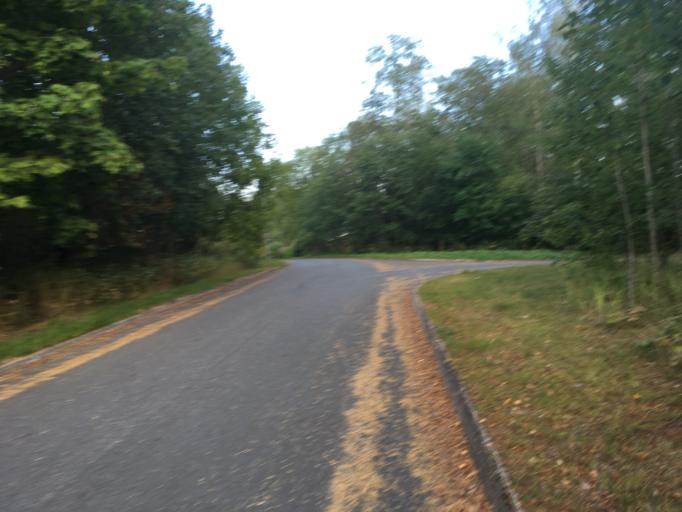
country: FI
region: Central Finland
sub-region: Jyvaeskylae
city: Jyvaeskylae
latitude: 62.2256
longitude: 25.7982
